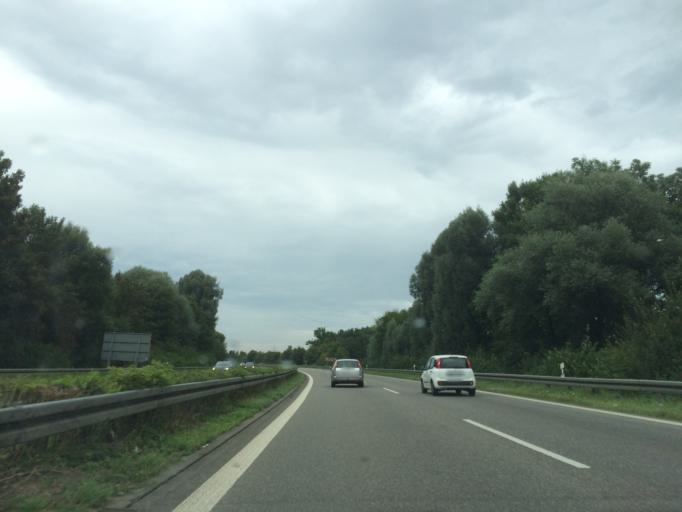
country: DE
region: Baden-Wuerttemberg
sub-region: Tuebingen Region
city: Berg
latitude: 47.8220
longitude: 9.6151
